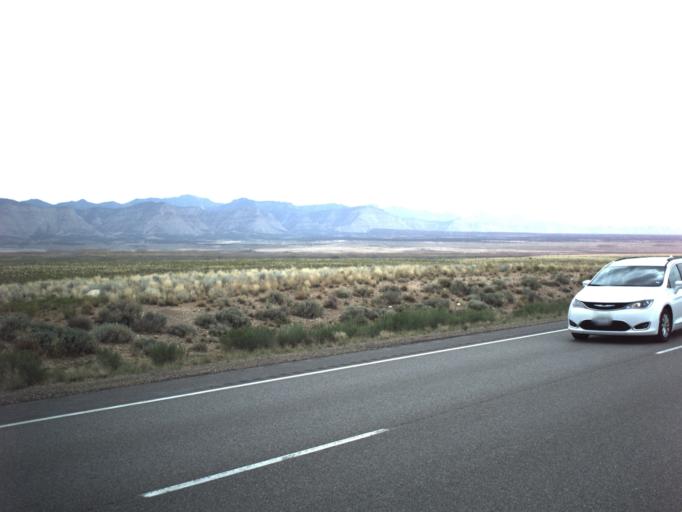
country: US
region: Utah
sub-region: Carbon County
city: East Carbon City
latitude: 39.4846
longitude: -110.5134
